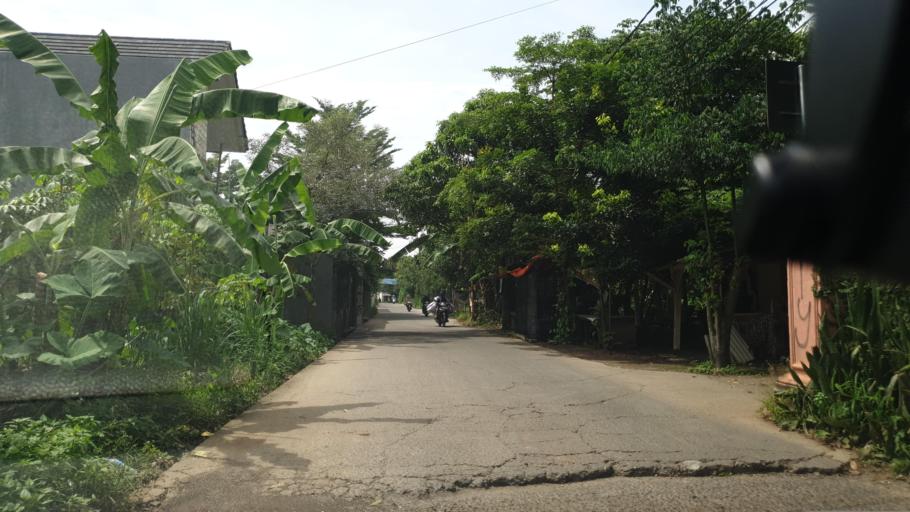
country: ID
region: West Java
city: Pamulang
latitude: -6.3646
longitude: 106.7640
